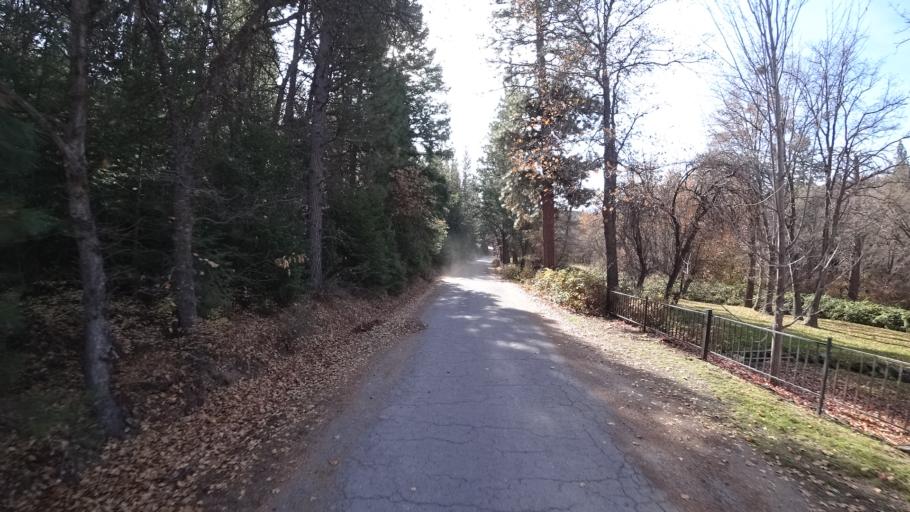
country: US
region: California
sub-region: Siskiyou County
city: Weed
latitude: 41.4434
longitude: -122.4240
